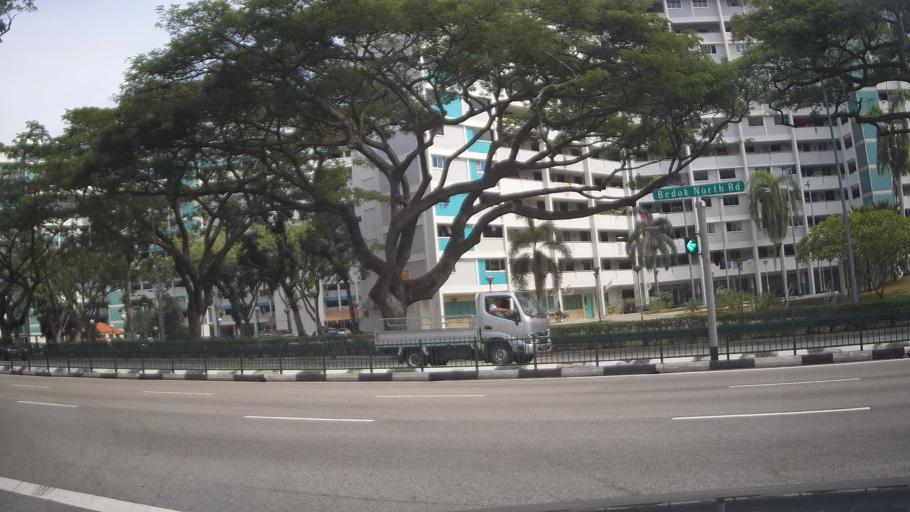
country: SG
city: Singapore
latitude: 1.3291
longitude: 103.9238
